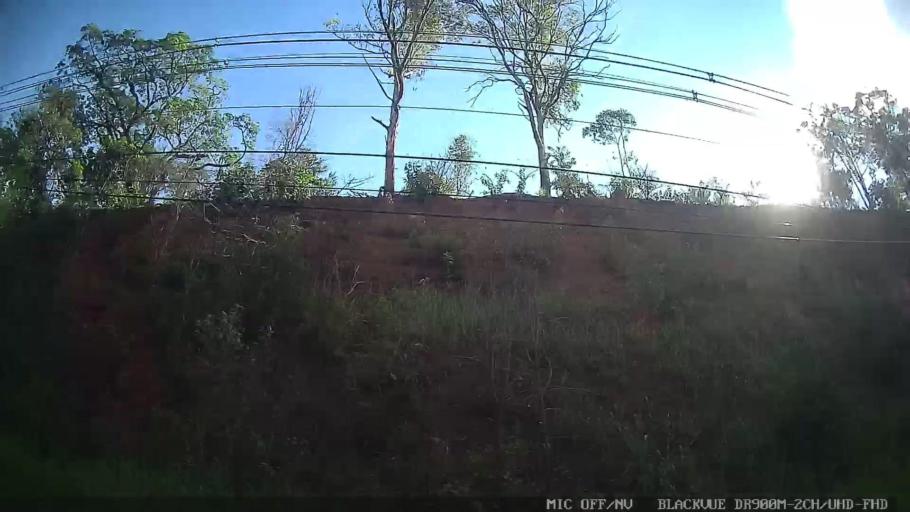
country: BR
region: Sao Paulo
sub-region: Serra Negra
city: Serra Negra
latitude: -22.6100
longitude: -46.7125
